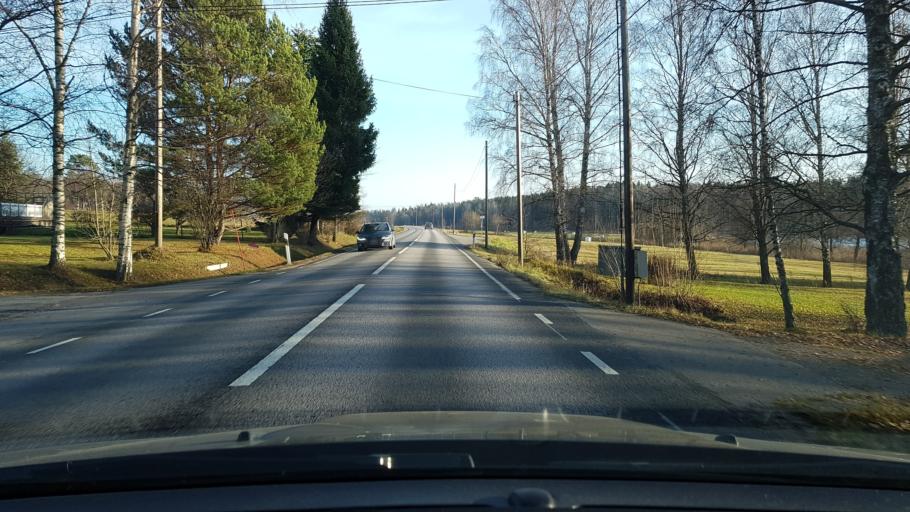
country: SE
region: Stockholm
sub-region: Norrtalje Kommun
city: Nykvarn
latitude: 59.7353
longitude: 18.2722
